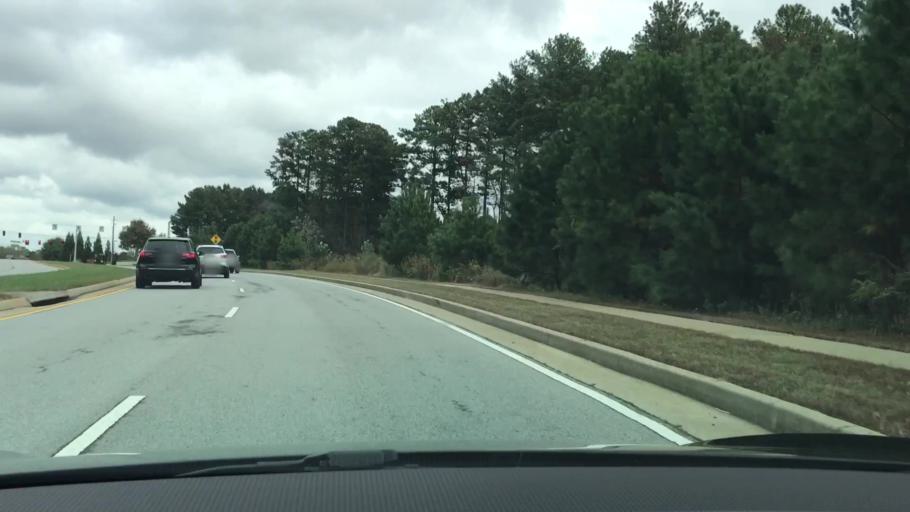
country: US
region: Georgia
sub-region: Gwinnett County
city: Suwanee
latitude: 34.0209
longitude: -84.0454
